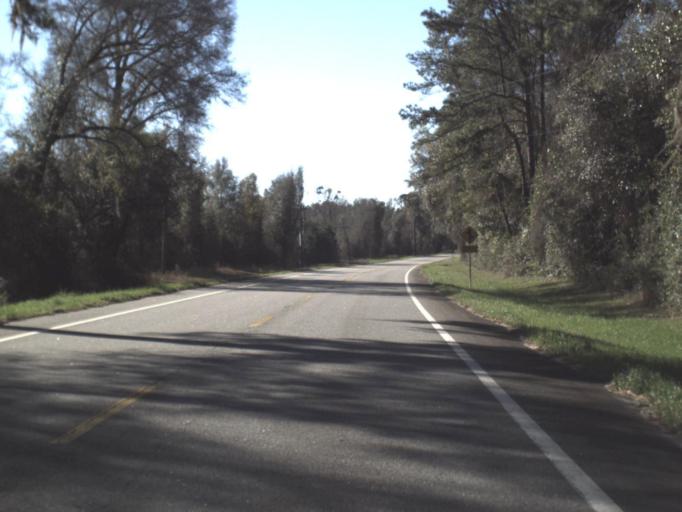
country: US
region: Georgia
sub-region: Brooks County
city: Quitman
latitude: 30.5823
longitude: -83.6374
